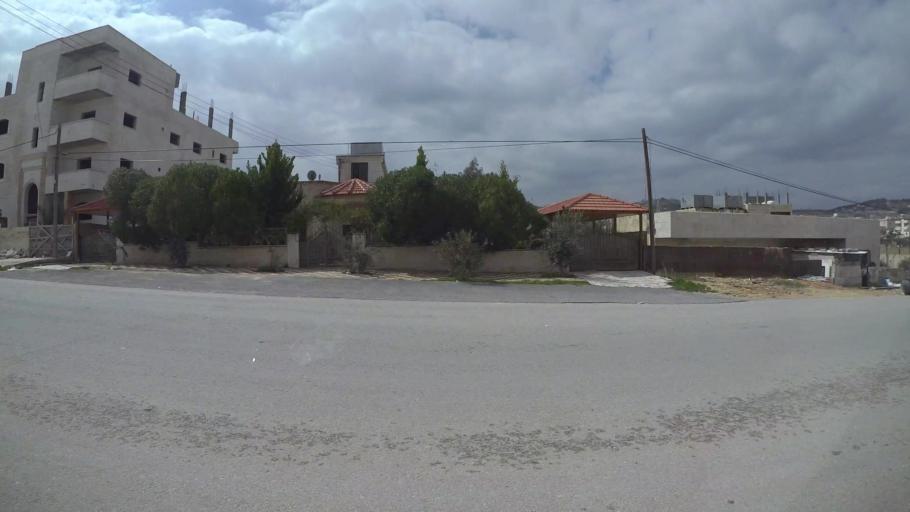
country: JO
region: Amman
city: Al Jubayhah
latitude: 32.0528
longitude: 35.8223
